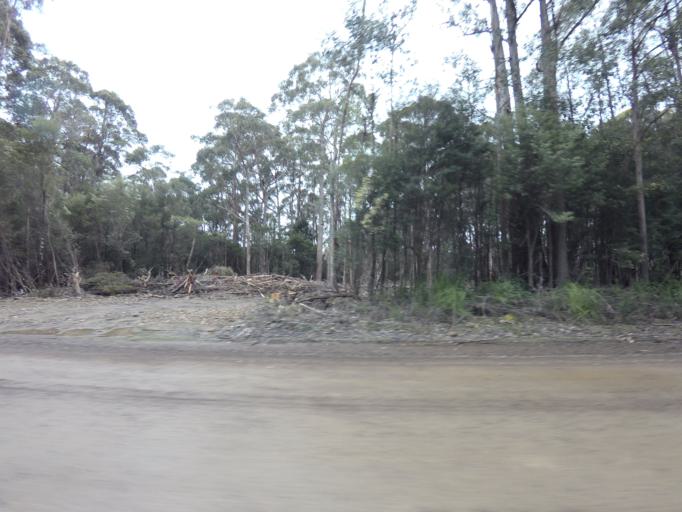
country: AU
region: Tasmania
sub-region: Huon Valley
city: Geeveston
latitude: -43.5161
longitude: 146.8858
